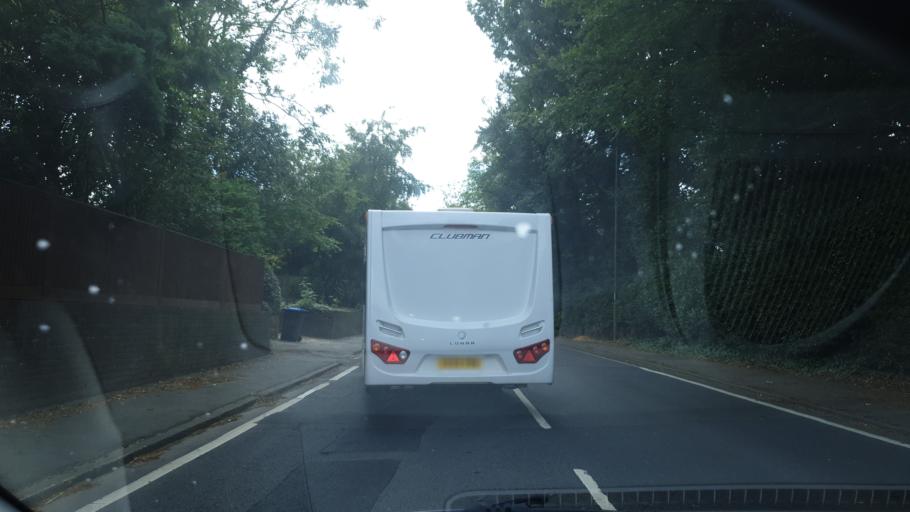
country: GB
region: England
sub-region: West Sussex
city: East Grinstead
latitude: 51.1209
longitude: 0.0071
